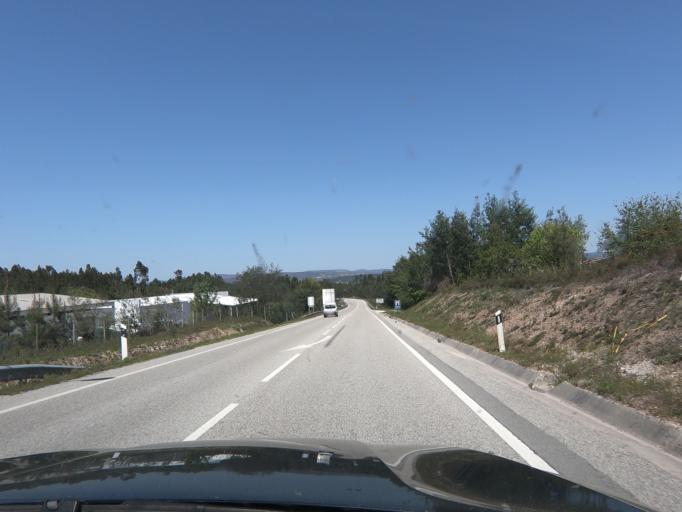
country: PT
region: Coimbra
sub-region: Lousa
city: Lousa
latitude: 40.1146
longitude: -8.2906
